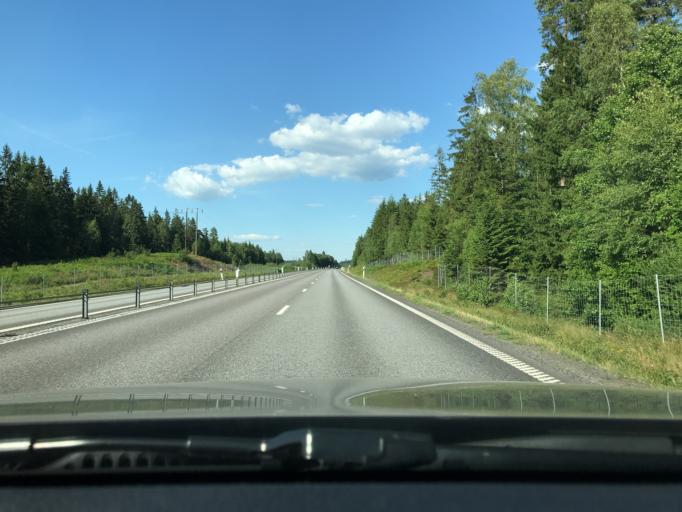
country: SE
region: Skane
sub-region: Osby Kommun
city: Osby
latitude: 56.4497
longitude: 14.0816
